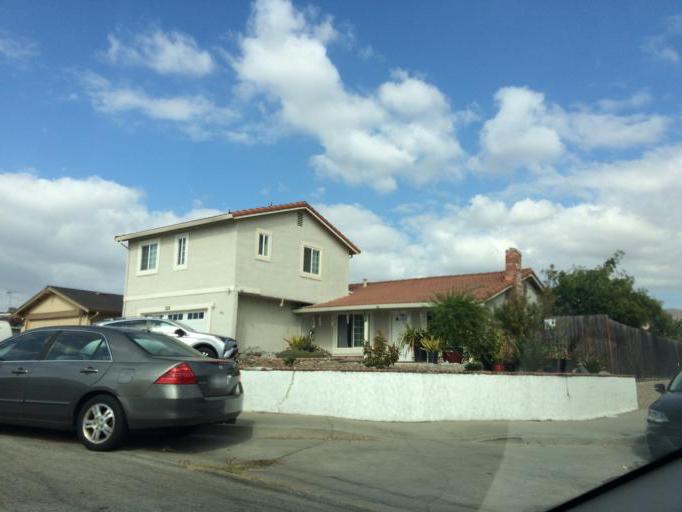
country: US
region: California
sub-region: Santa Clara County
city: Alum Rock
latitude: 37.3688
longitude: -121.8491
